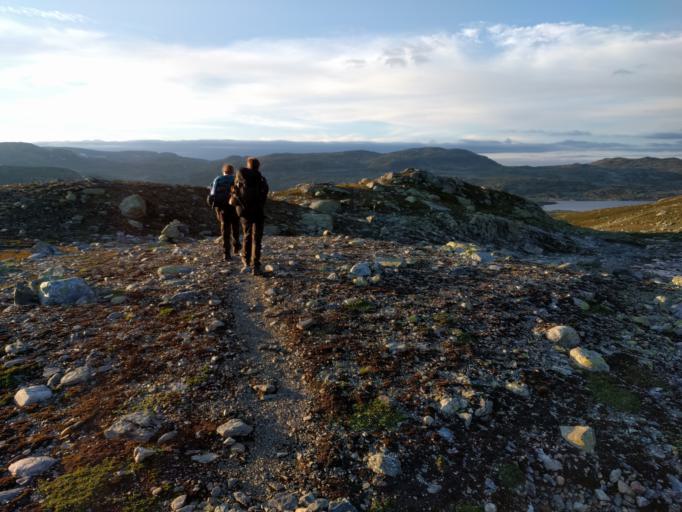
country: NO
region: Aust-Agder
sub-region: Bykle
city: Hovden
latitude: 59.9677
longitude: 7.2153
